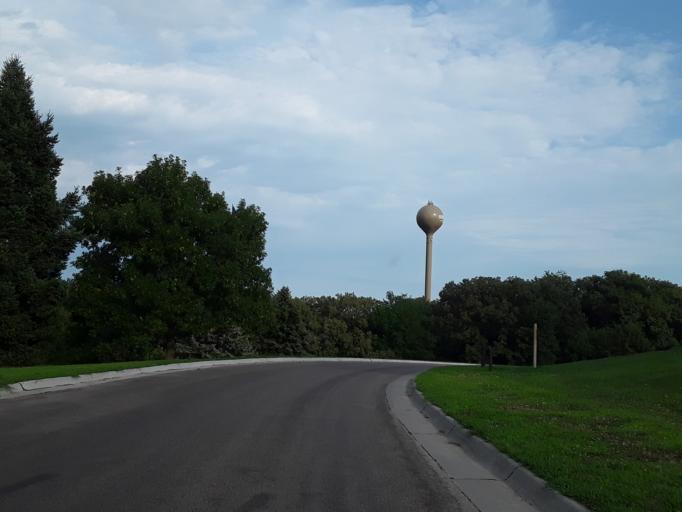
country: US
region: Nebraska
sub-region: Saunders County
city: Ashland
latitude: 41.0273
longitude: -96.3099
